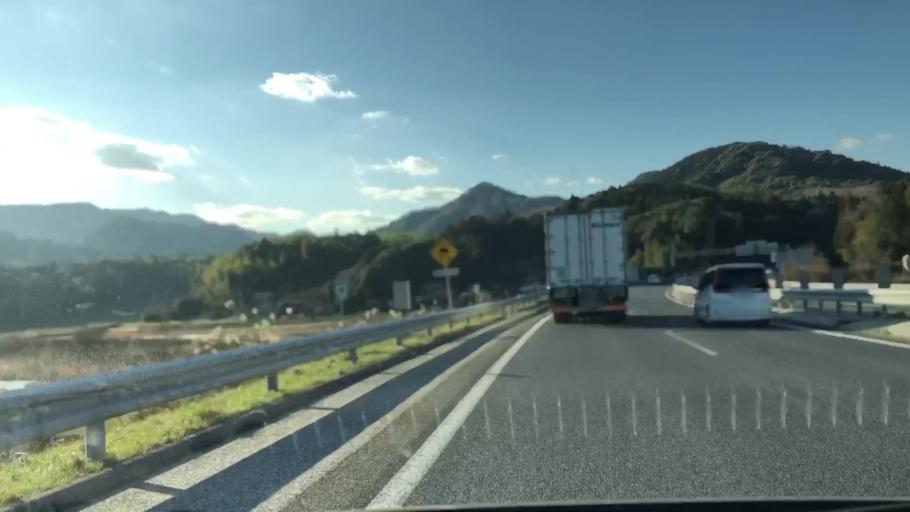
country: JP
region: Yamaguchi
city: Ogori-shimogo
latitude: 34.1727
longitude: 131.3145
